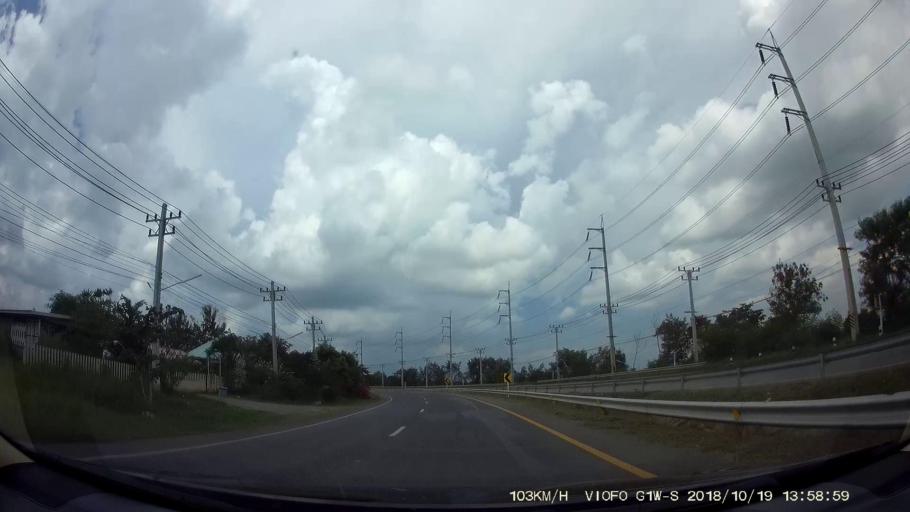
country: TH
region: Chaiyaphum
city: Chaiyaphum
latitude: 15.8033
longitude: 102.0604
